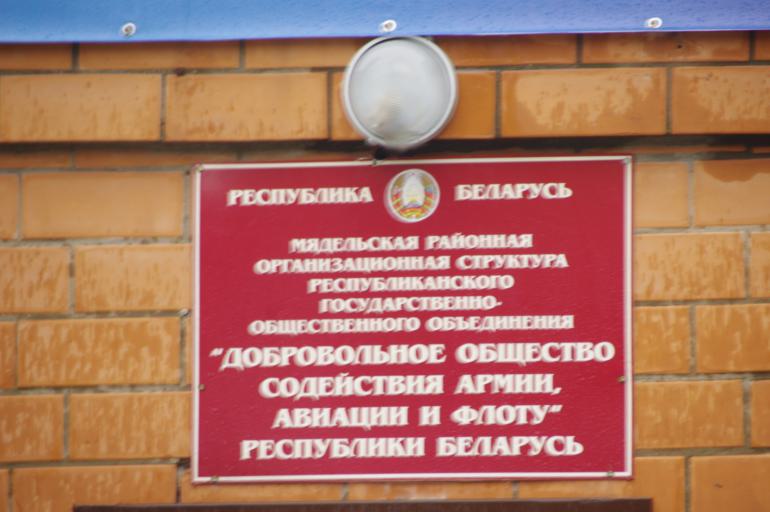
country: BY
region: Minsk
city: Narach
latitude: 54.9094
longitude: 26.7072
